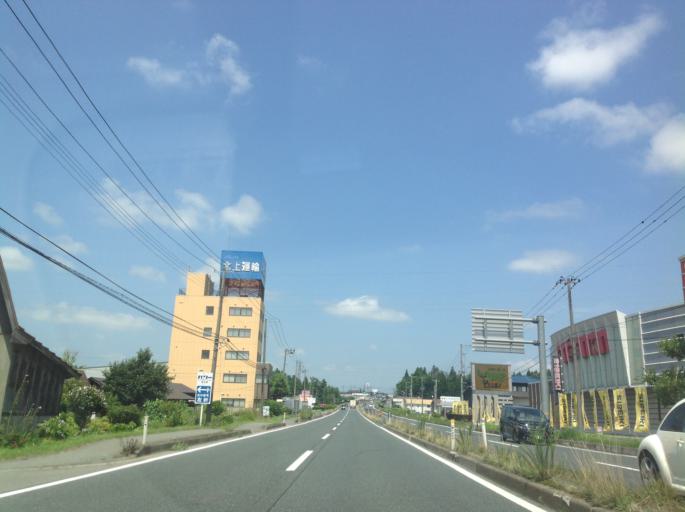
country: JP
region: Iwate
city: Kitakami
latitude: 39.3016
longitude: 141.1079
